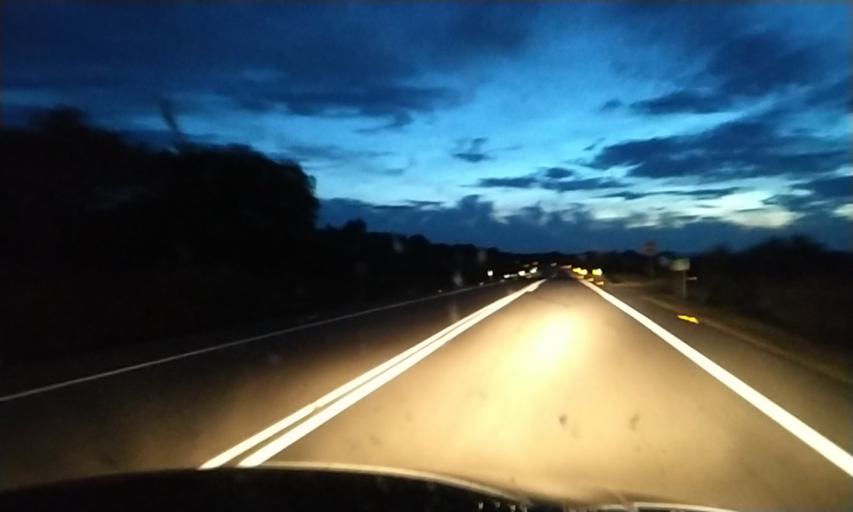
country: ES
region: Extremadura
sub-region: Provincia de Caceres
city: Carcaboso
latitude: 39.9789
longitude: -6.1934
